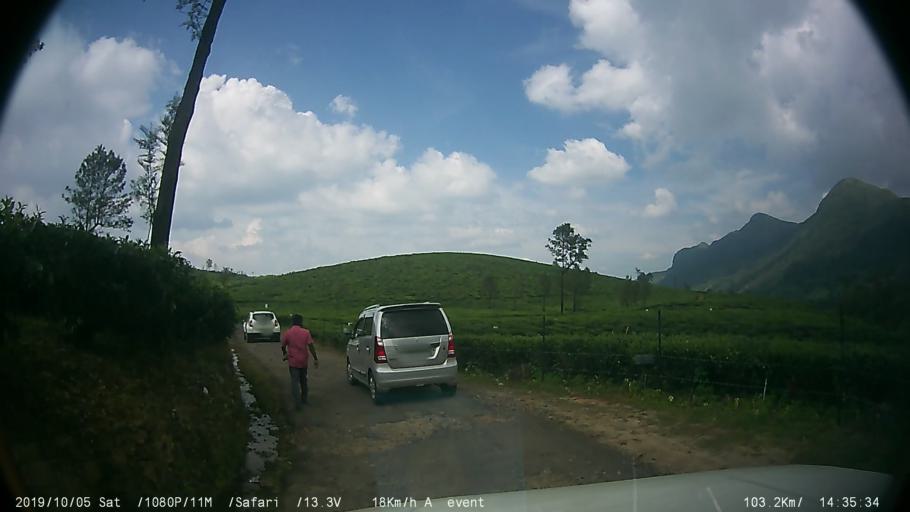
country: IN
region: Kerala
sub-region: Kottayam
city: Erattupetta
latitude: 9.6173
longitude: 76.9619
